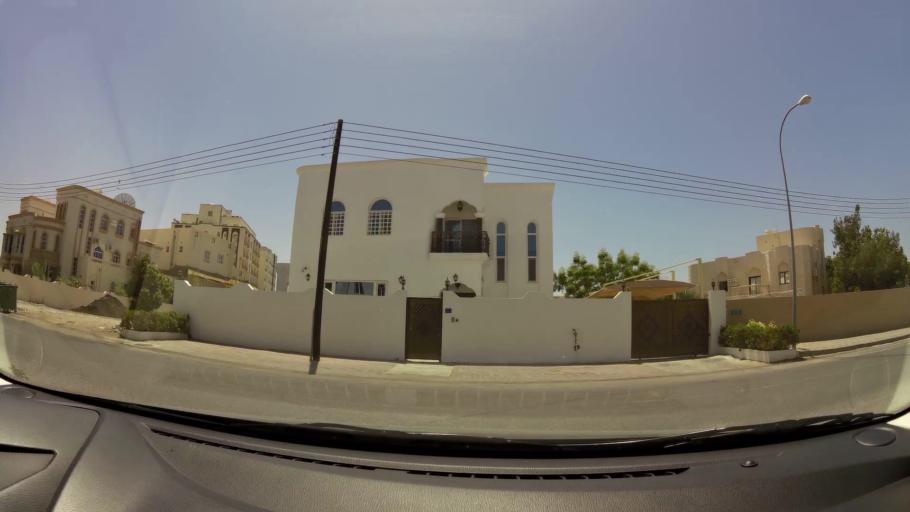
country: OM
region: Muhafazat Masqat
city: Bawshar
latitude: 23.5935
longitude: 58.3757
